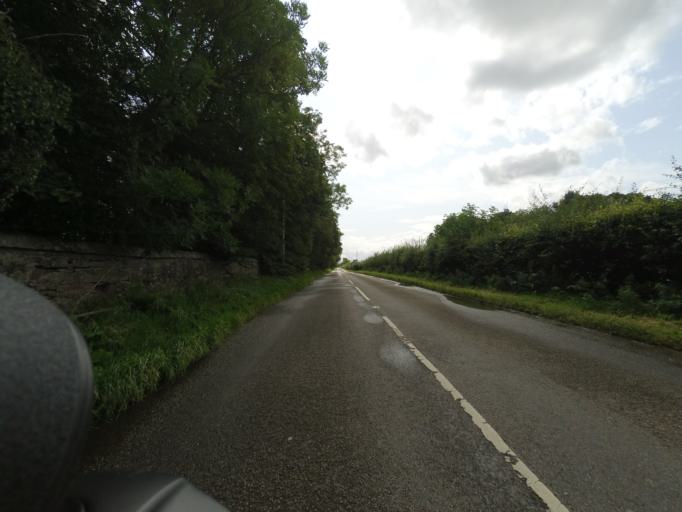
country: GB
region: Scotland
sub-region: Highland
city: Tain
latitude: 57.7396
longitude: -4.0800
